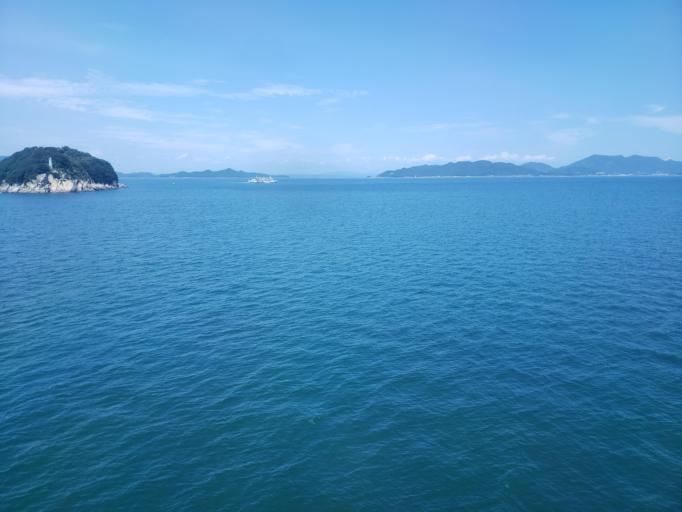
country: JP
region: Kagawa
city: Tonosho
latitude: 34.4055
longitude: 134.1415
